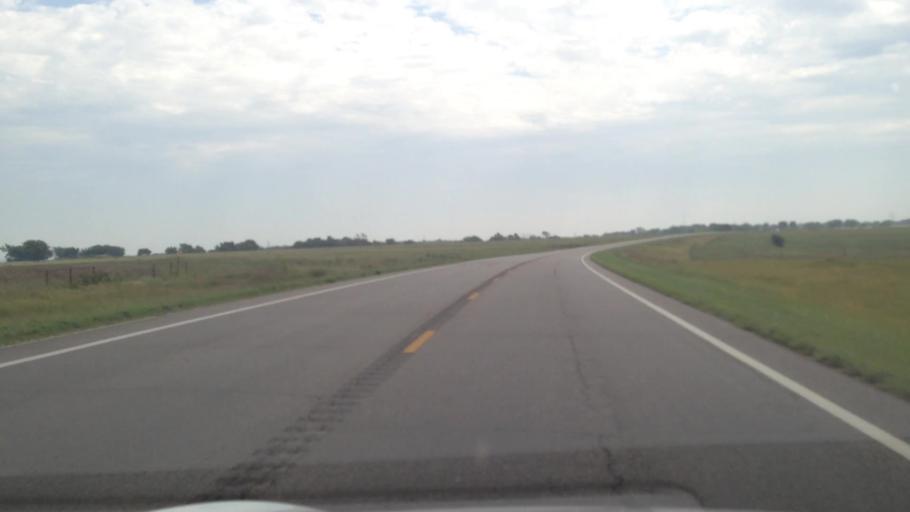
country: US
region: Kansas
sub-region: Bourbon County
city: Fort Scott
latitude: 37.8821
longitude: -95.0117
